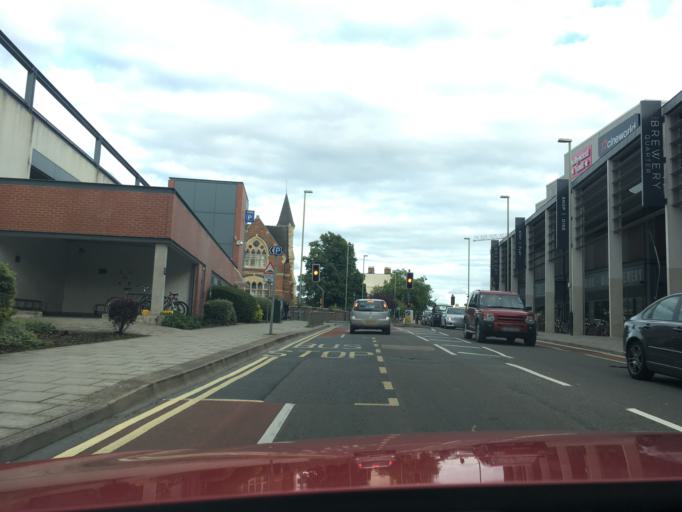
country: GB
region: England
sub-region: Gloucestershire
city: Cheltenham
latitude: 51.9042
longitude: -2.0761
